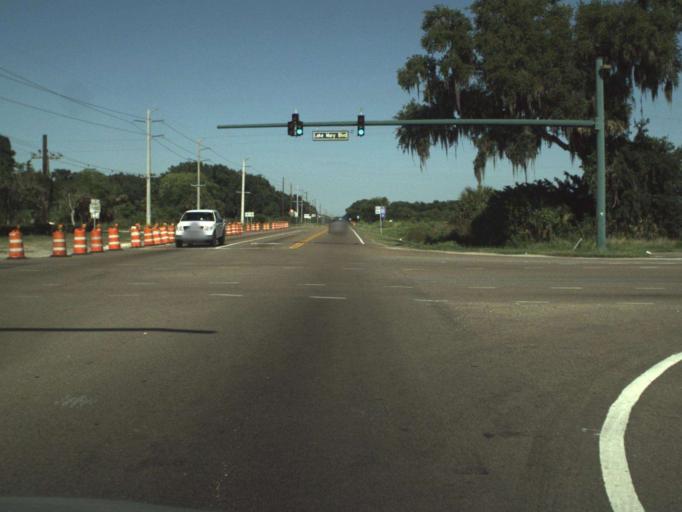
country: US
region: Florida
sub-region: Seminole County
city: Midway
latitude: 28.7868
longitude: -81.2130
